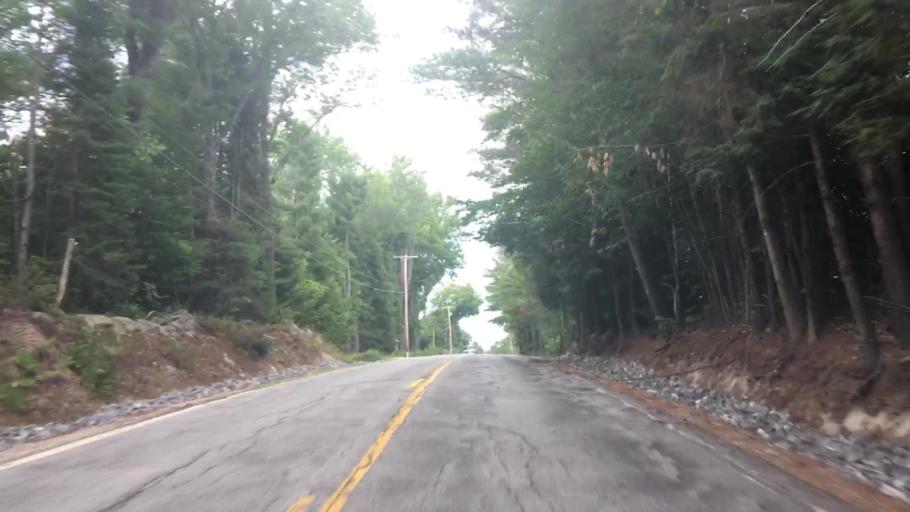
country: US
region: Maine
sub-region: Oxford County
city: Oxford
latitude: 44.0643
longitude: -70.5475
